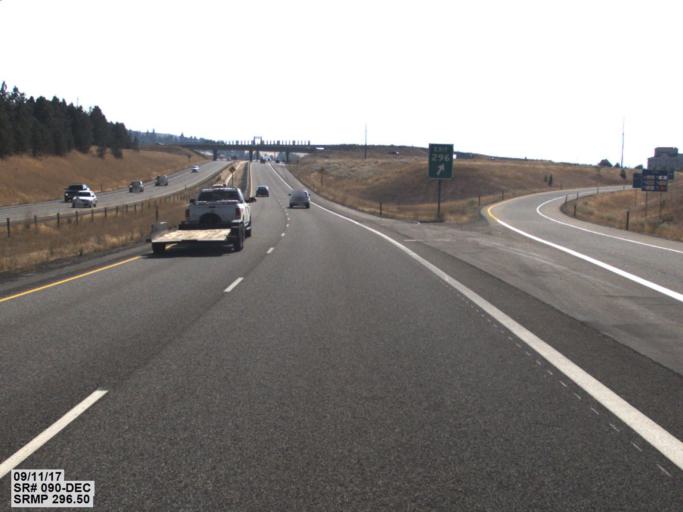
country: US
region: Washington
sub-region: Spokane County
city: Liberty Lake
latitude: 47.6763
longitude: -117.1054
